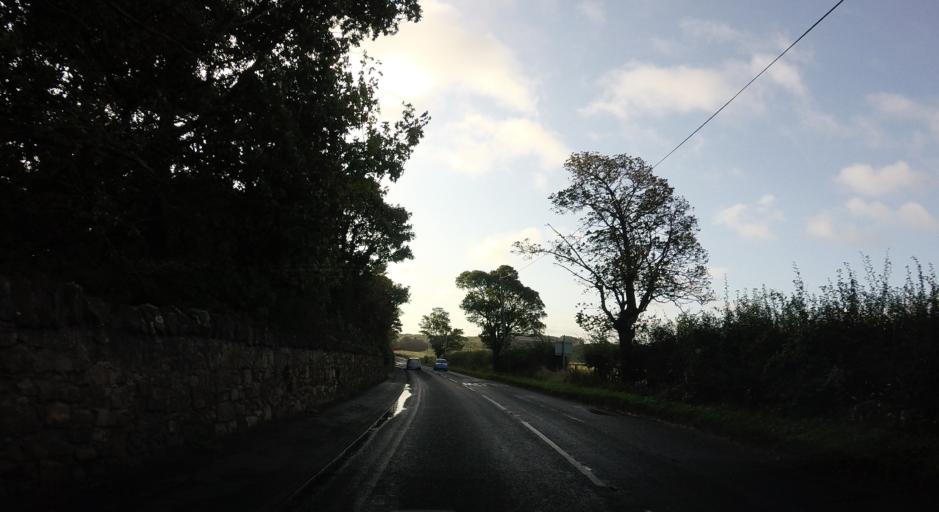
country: GB
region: Scotland
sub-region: East Lothian
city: Musselburgh
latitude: 55.9144
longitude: -3.0257
